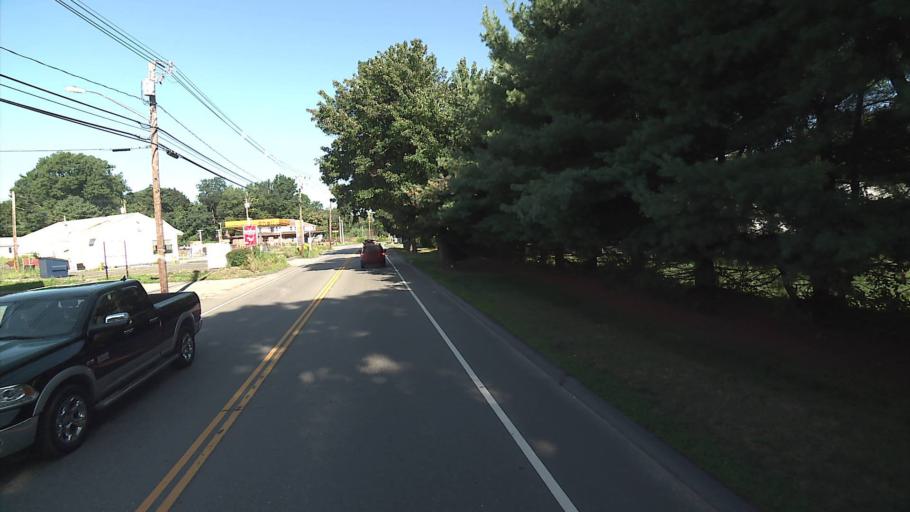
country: US
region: Connecticut
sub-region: Middlesex County
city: Clinton
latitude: 41.2735
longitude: -72.5085
